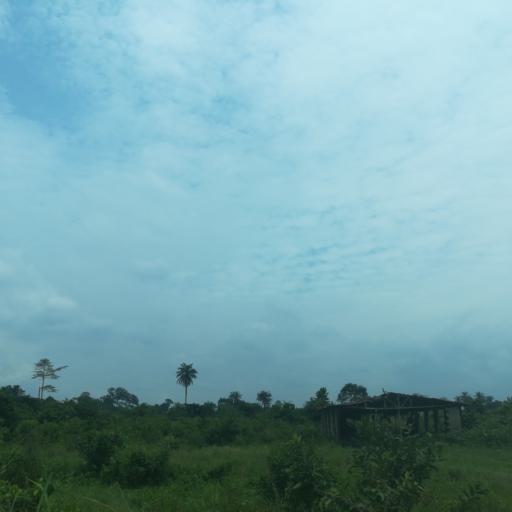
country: NG
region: Lagos
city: Ejirin
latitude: 6.6773
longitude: 3.8002
